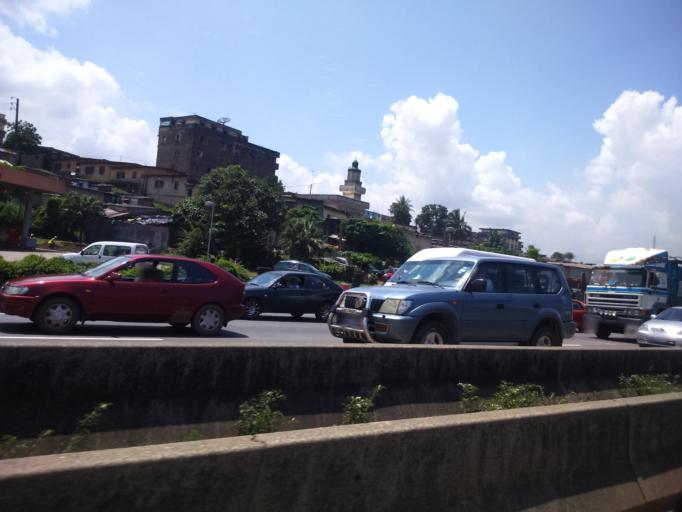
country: CI
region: Lagunes
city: Abidjan
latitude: 5.3619
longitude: -4.0232
